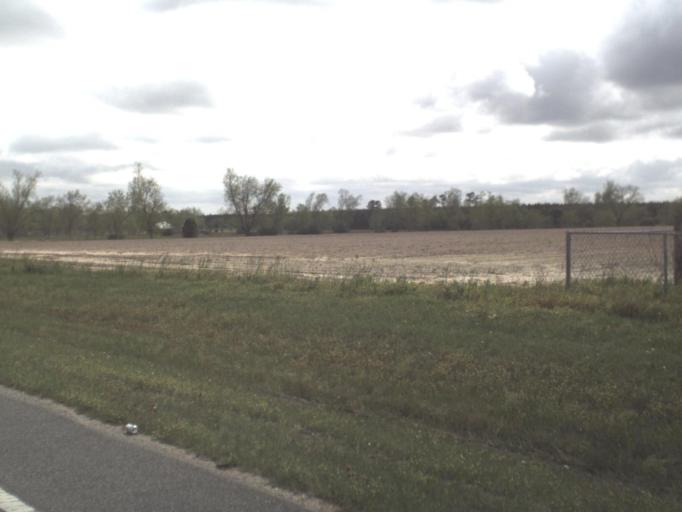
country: US
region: Florida
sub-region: Santa Rosa County
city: Point Baker
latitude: 30.7552
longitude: -87.0933
